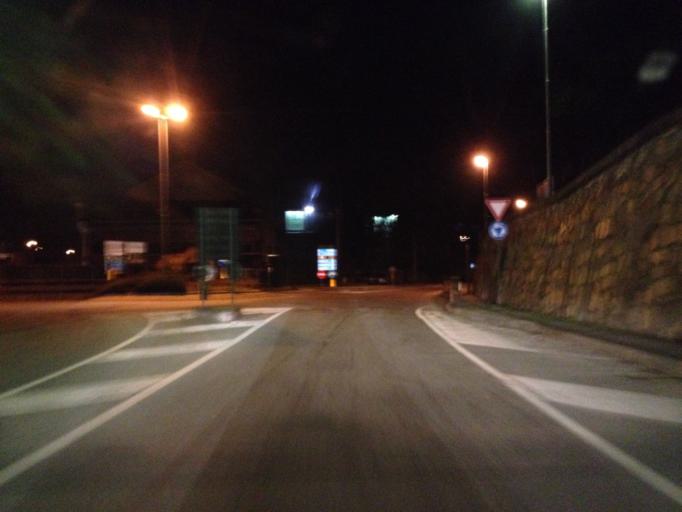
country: IT
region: Piedmont
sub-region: Provincia di Torino
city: San Mauro Torinese
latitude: 45.1043
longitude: 7.7675
